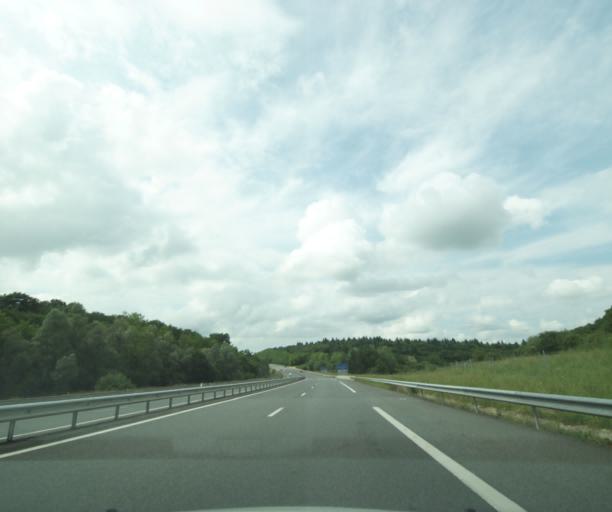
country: FR
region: Centre
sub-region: Departement du Cher
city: Orval
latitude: 46.7421
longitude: 2.4270
